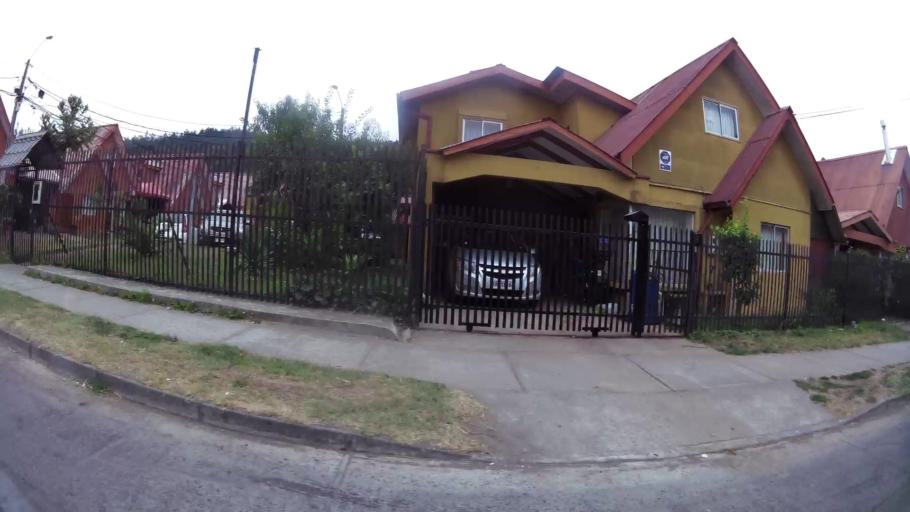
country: CL
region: Biobio
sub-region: Provincia de Concepcion
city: Concepcion
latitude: -36.8318
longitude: -73.0104
